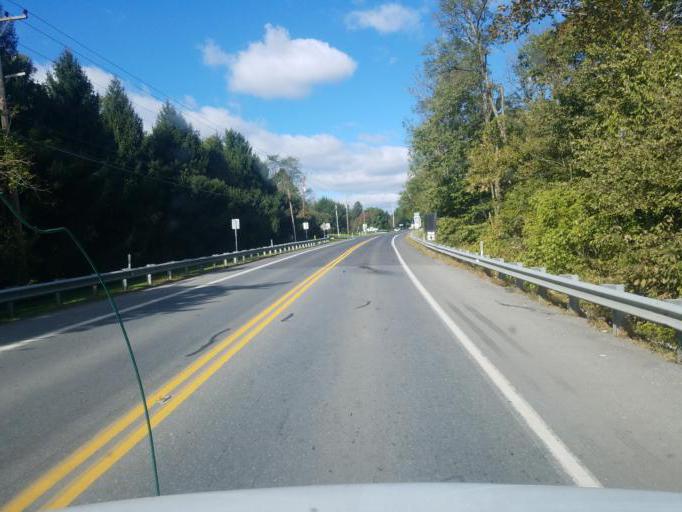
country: US
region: Pennsylvania
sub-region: Franklin County
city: Mercersburg
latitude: 39.8043
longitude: -77.8708
